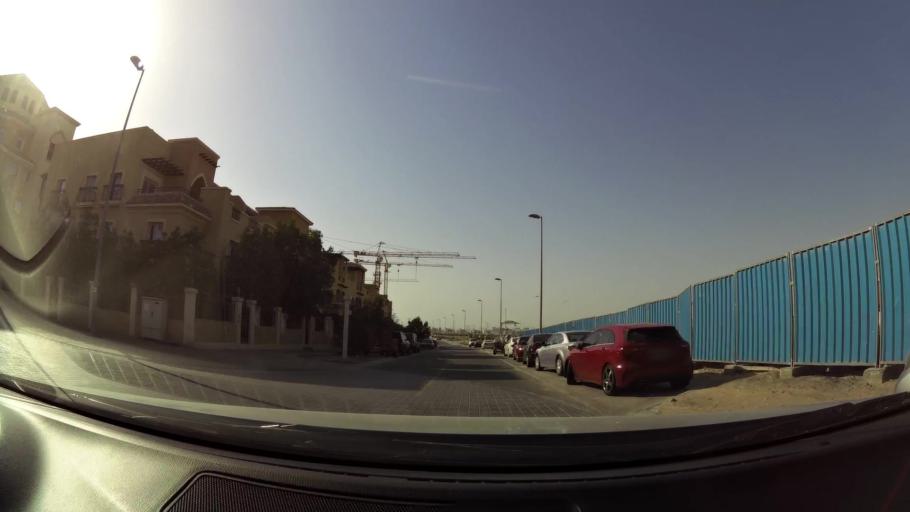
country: AE
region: Dubai
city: Dubai
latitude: 25.0641
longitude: 55.2172
